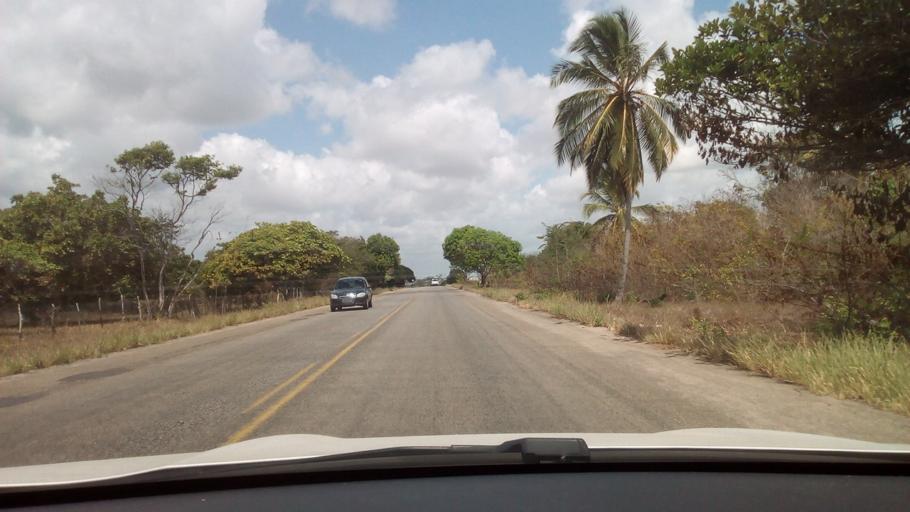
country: BR
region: Paraiba
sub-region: Conde
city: Conde
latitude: -7.2485
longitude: -34.8281
